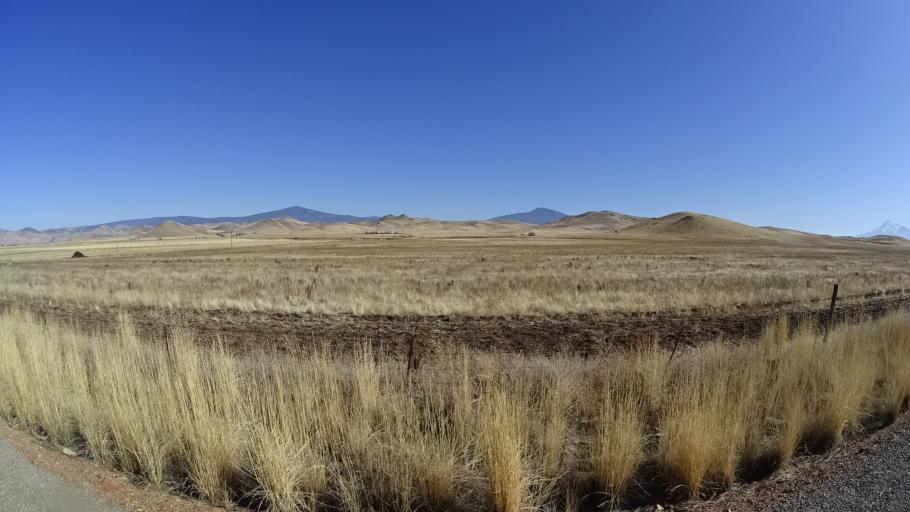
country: US
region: California
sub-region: Siskiyou County
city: Montague
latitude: 41.7585
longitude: -122.4570
